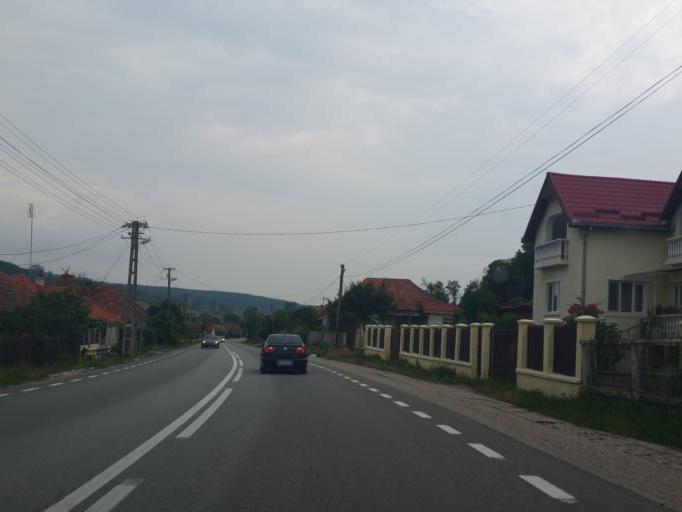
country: RO
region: Salaj
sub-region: Comuna Sanmihaiu Almasului
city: Sanmihaiu Almasului
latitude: 46.9575
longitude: 23.3414
